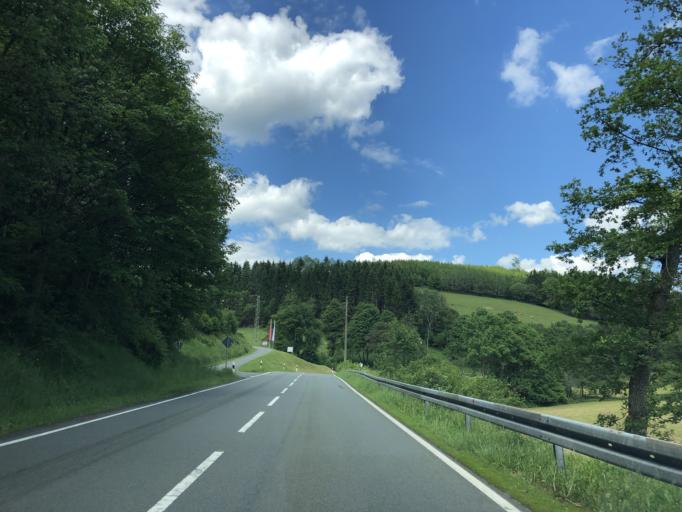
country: DE
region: North Rhine-Westphalia
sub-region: Regierungsbezirk Arnsberg
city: Winterberg
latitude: 51.1863
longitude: 8.4311
